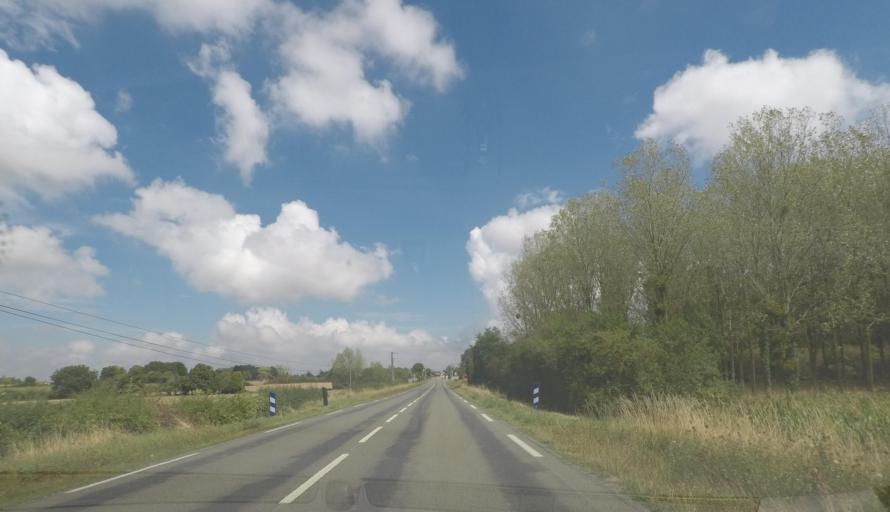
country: FR
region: Pays de la Loire
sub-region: Departement de la Sarthe
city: Saint-Cosme-en-Vairais
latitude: 48.2679
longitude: 0.4504
